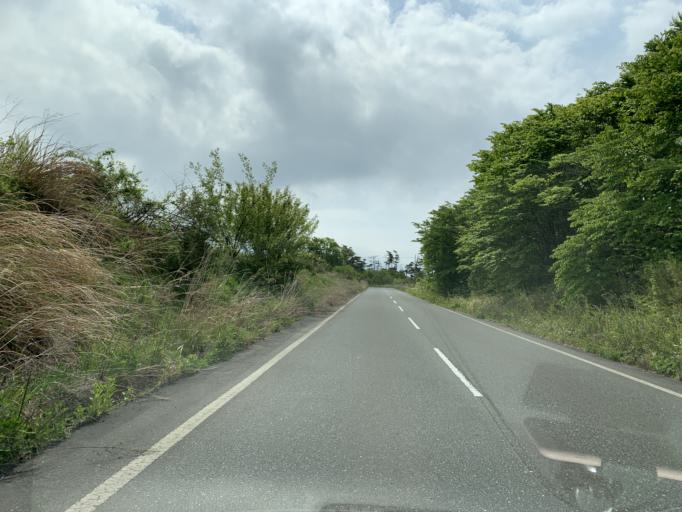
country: JP
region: Iwate
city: Ichinoseki
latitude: 38.8422
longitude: 141.2125
